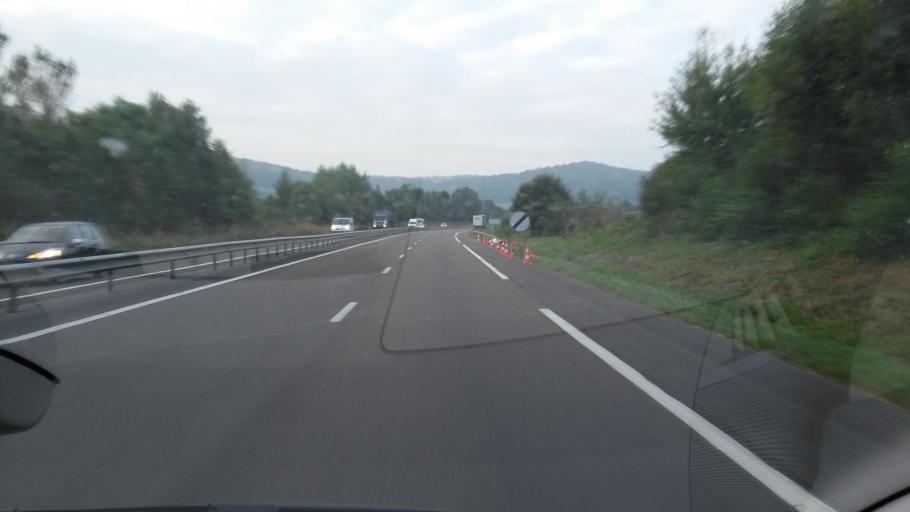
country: FR
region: Champagne-Ardenne
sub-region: Departement des Ardennes
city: La Francheville
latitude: 49.7030
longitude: 4.6967
